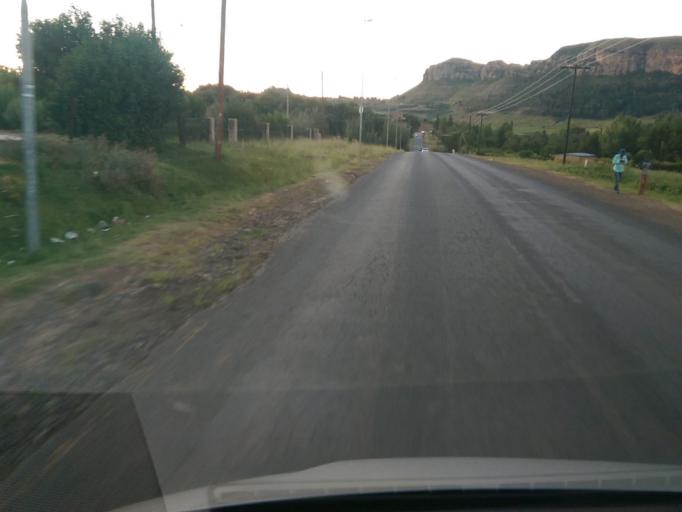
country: LS
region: Maseru
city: Nako
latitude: -29.4435
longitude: 27.7093
